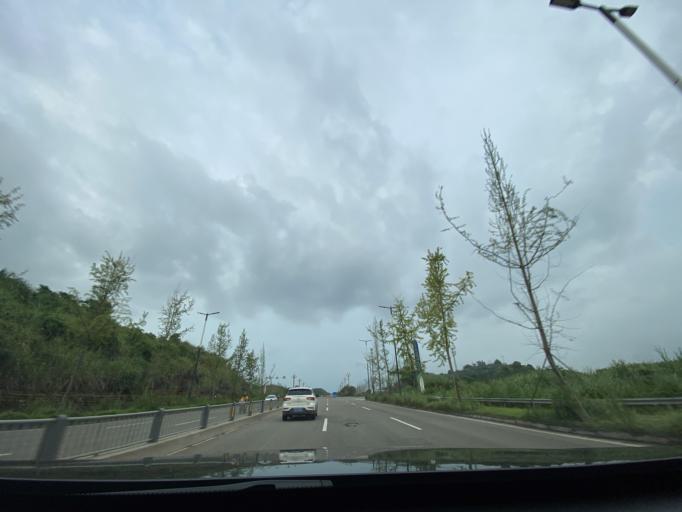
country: CN
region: Sichuan
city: Jiancheng
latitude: 30.4877
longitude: 104.4750
